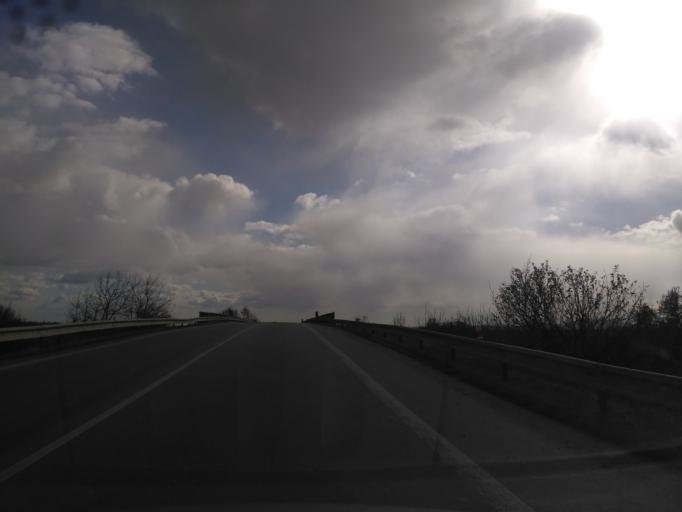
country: SK
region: Kosicky
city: Trebisov
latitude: 48.6267
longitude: 21.6966
